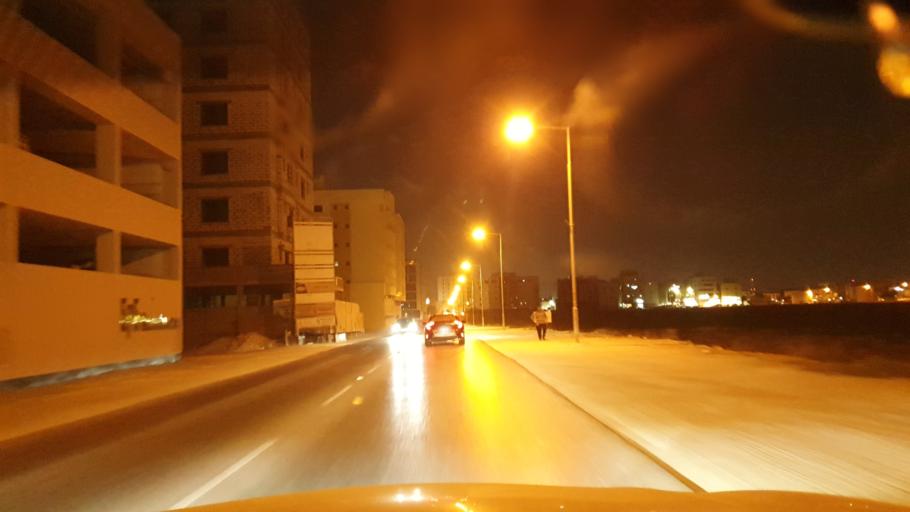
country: BH
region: Northern
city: Madinat `Isa
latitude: 26.1857
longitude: 50.4820
